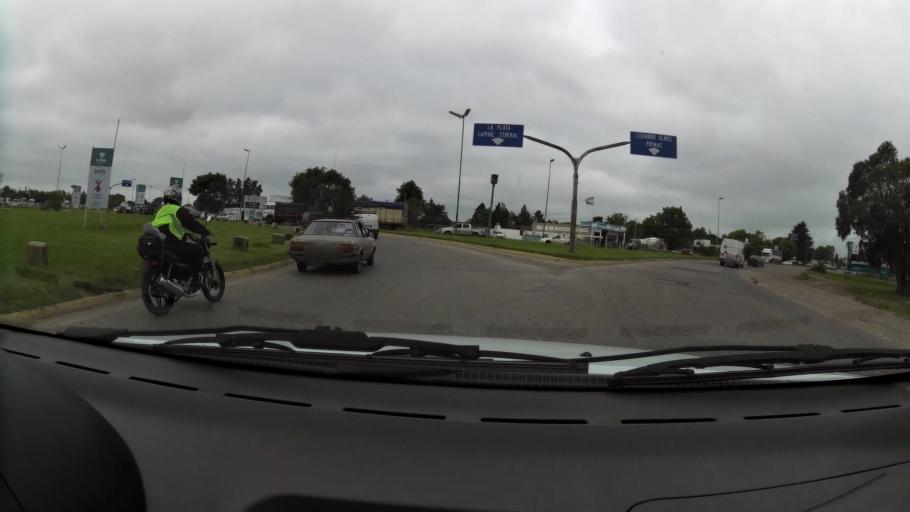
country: AR
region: Buenos Aires
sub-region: Partido de La Plata
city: La Plata
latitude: -34.9902
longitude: -58.0420
